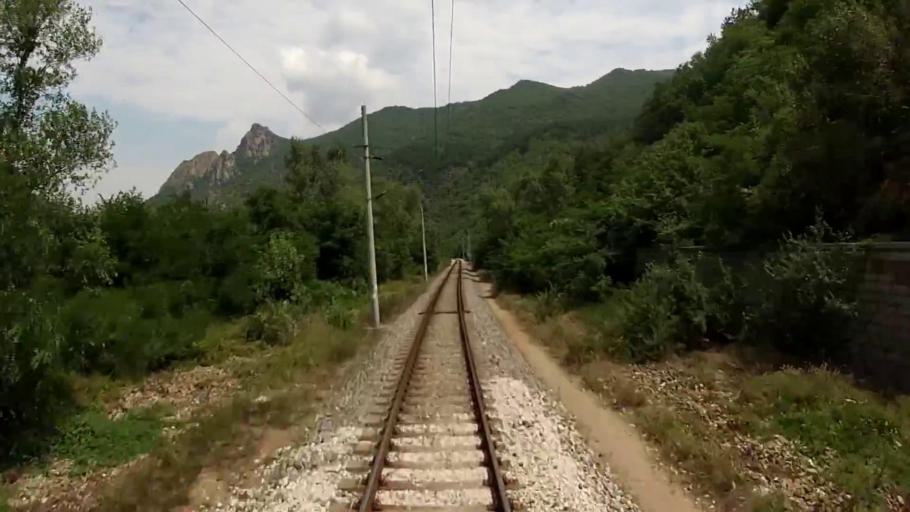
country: BG
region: Blagoevgrad
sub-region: Obshtina Kresna
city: Stara Kresna
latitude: 41.7923
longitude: 23.1623
